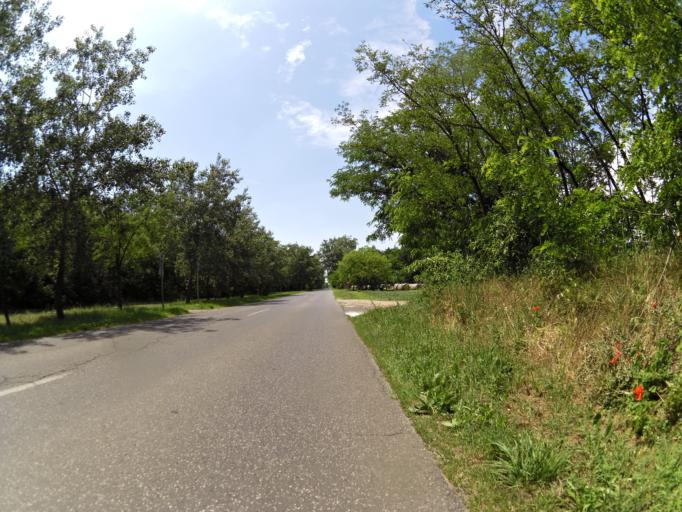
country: HU
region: Csongrad
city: Opusztaszer
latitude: 46.4933
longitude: 20.0422
